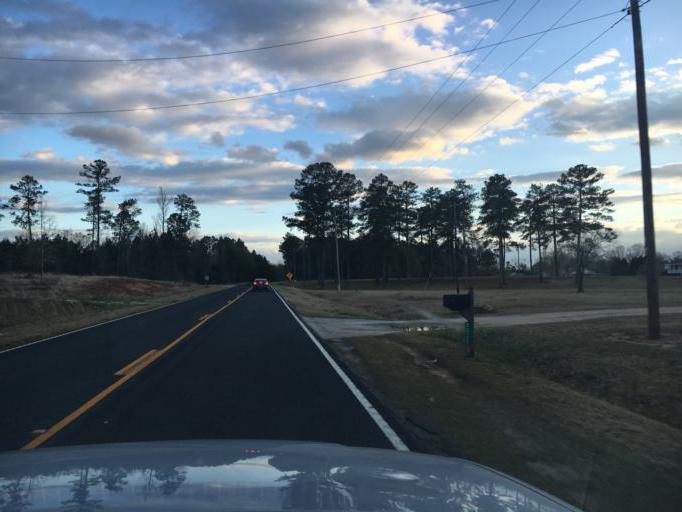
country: US
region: South Carolina
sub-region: Greenwood County
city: Greenwood
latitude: 34.0996
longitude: -82.1876
